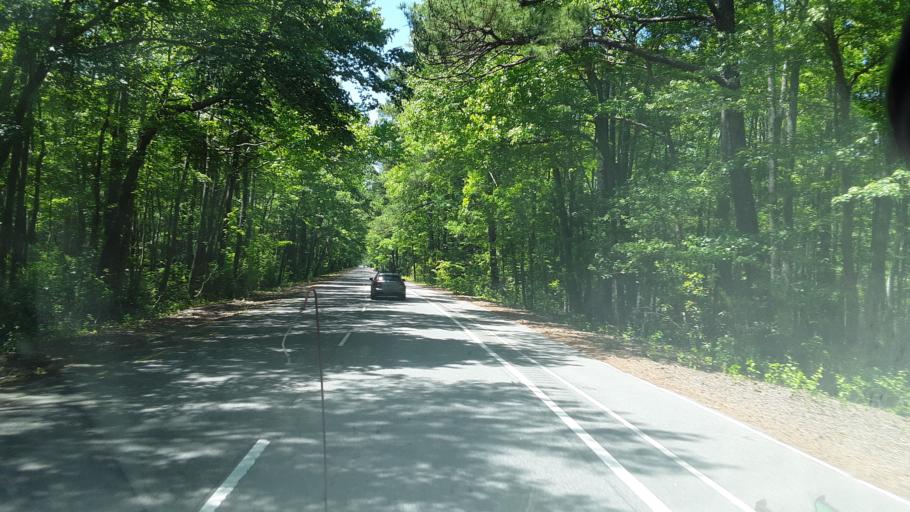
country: US
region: Virginia
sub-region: City of Virginia Beach
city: Virginia Beach
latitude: 36.9200
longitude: -76.0225
